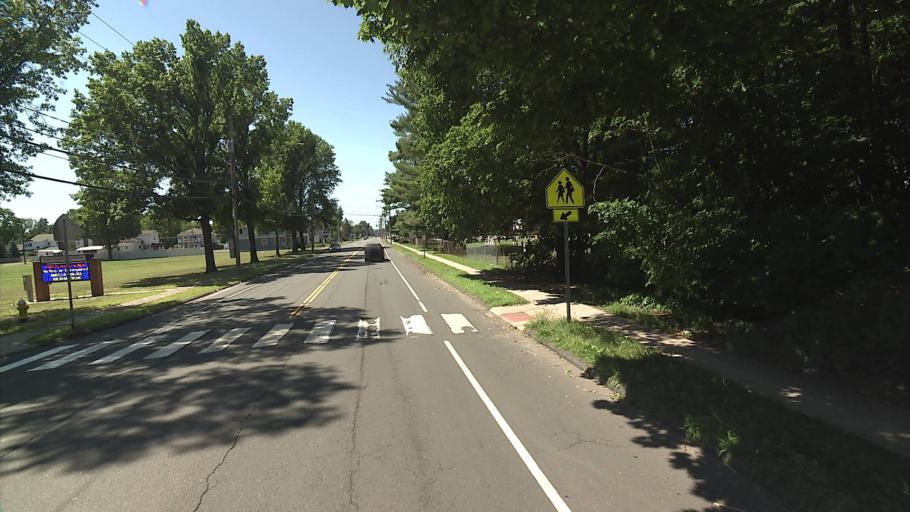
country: US
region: Connecticut
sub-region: Hartford County
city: Plainville
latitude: 41.6676
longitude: -72.8619
